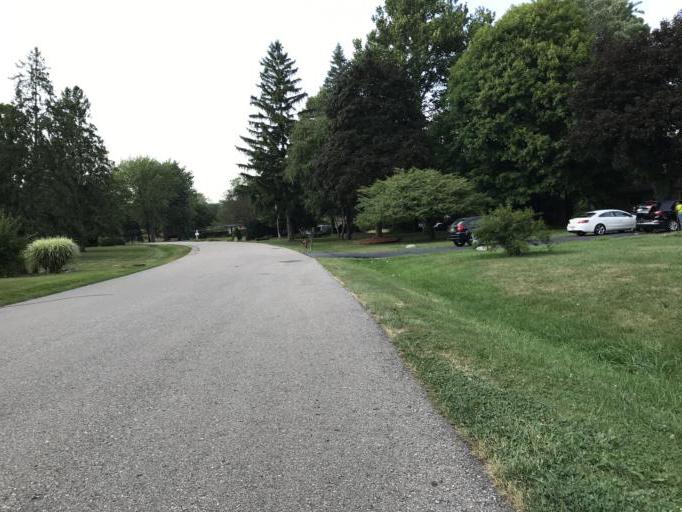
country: US
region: Michigan
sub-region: Oakland County
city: Farmington Hills
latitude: 42.4855
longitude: -83.3530
